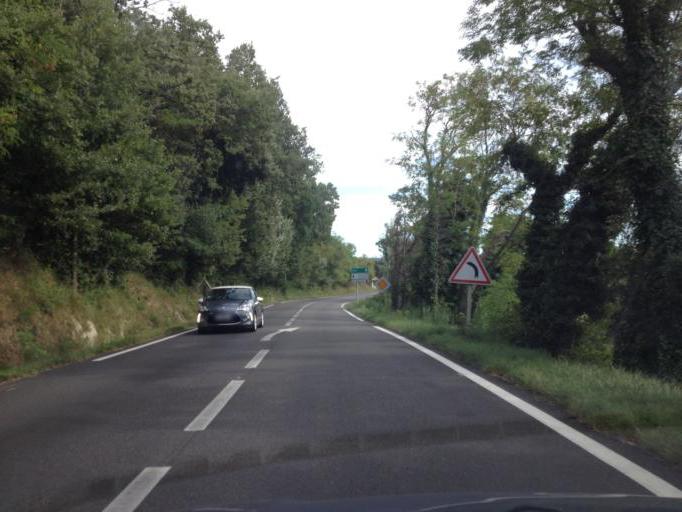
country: FR
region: Provence-Alpes-Cote d'Azur
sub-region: Departement du Vaucluse
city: Grillon
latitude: 44.3994
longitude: 4.9192
